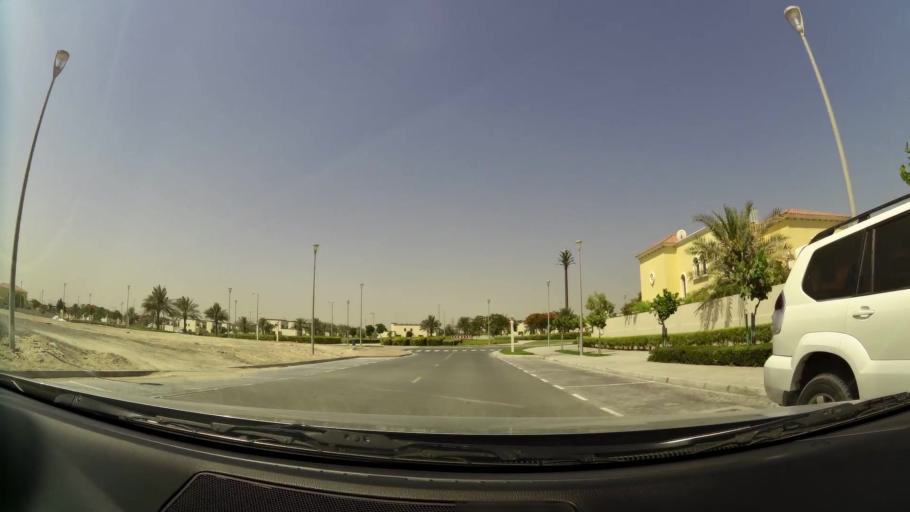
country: AE
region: Dubai
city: Dubai
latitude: 25.0512
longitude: 55.1518
